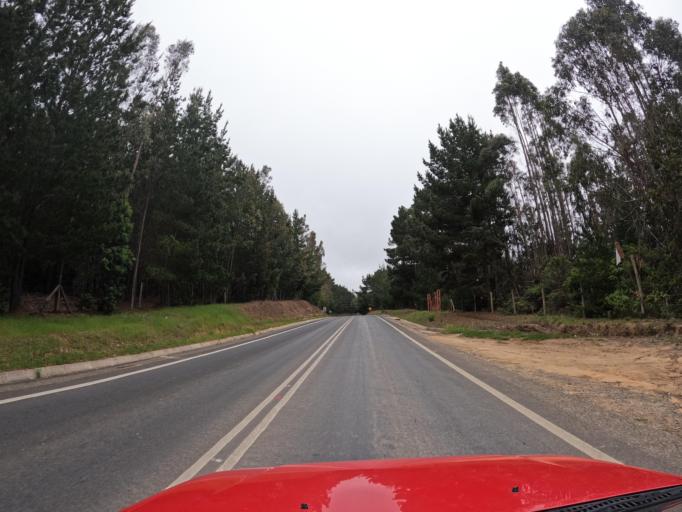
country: CL
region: O'Higgins
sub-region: Provincia de Colchagua
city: Santa Cruz
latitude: -34.6054
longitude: -72.0153
